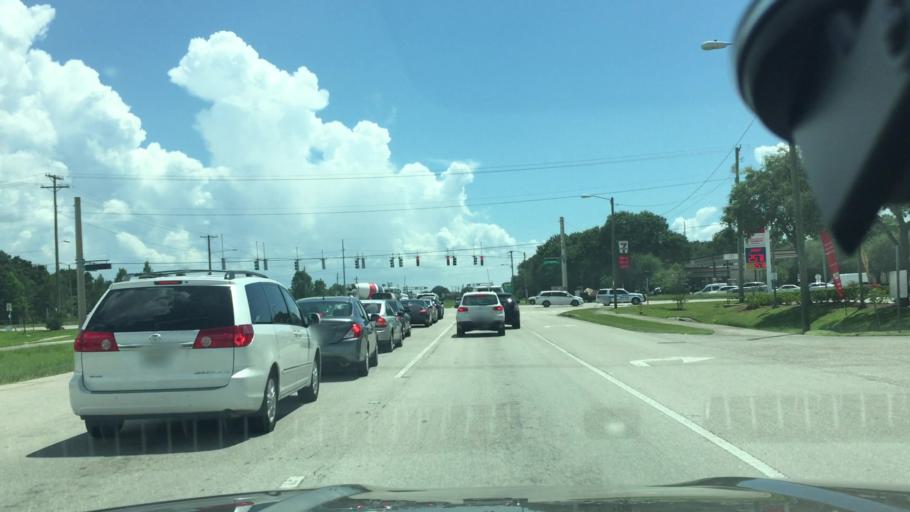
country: US
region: Florida
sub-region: Hillsborough County
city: Carrollwood Village
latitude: 28.0412
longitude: -82.5420
